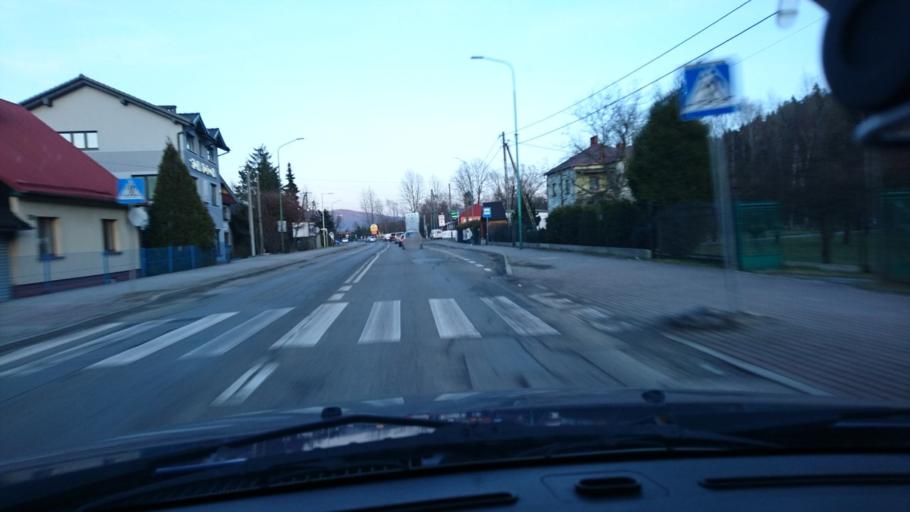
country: PL
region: Silesian Voivodeship
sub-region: Powiat bielski
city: Szczyrk
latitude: 49.7213
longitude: 19.0437
